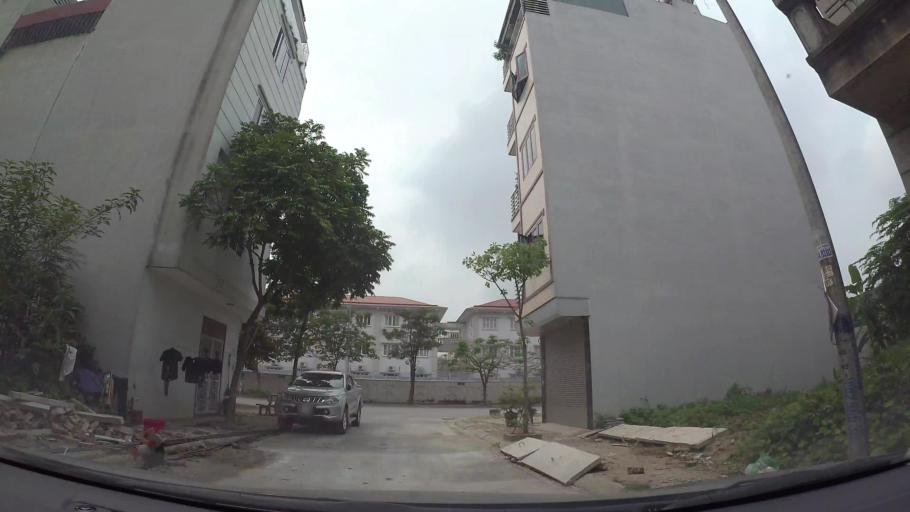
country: VN
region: Ha Noi
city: Trau Quy
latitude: 21.0641
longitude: 105.9169
